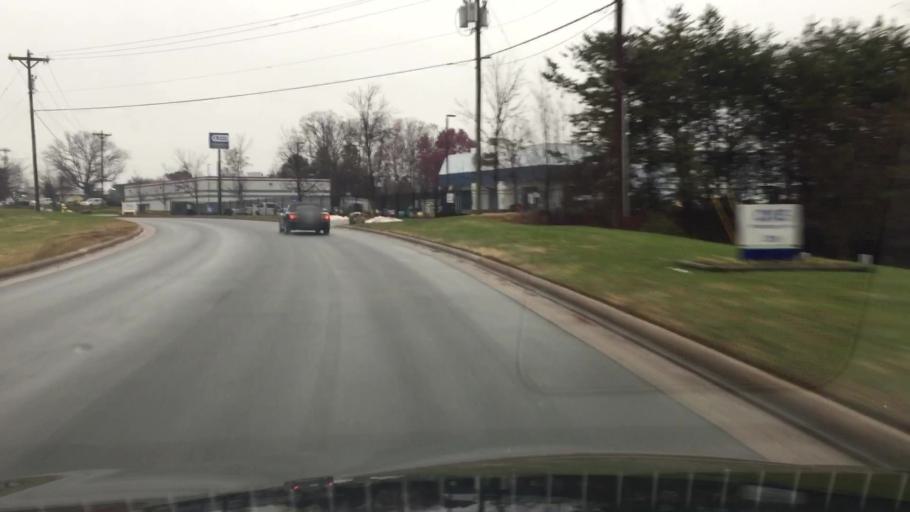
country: US
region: North Carolina
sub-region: Iredell County
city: Mooresville
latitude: 35.5842
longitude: -80.8602
